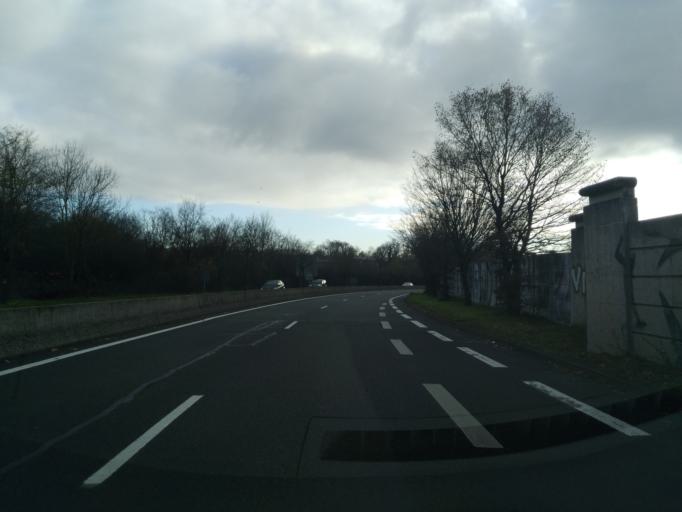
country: FR
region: Ile-de-France
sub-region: Departement des Yvelines
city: Buc
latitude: 48.7837
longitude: 2.1062
